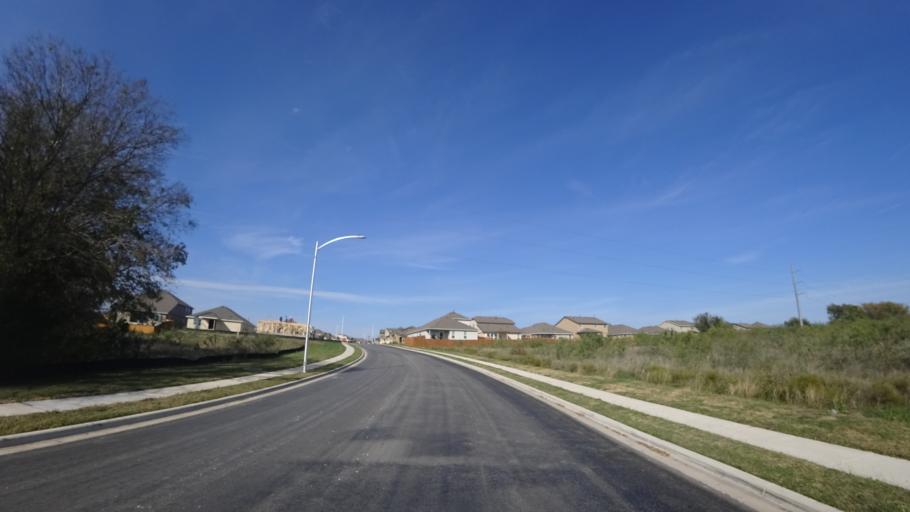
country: US
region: Texas
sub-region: Travis County
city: Pflugerville
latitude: 30.4074
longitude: -97.6406
